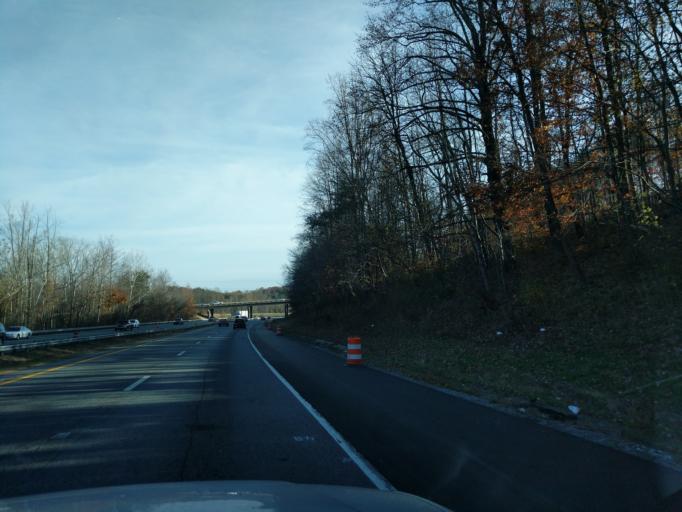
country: US
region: North Carolina
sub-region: Polk County
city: Columbus
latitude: 35.2474
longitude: -82.2072
